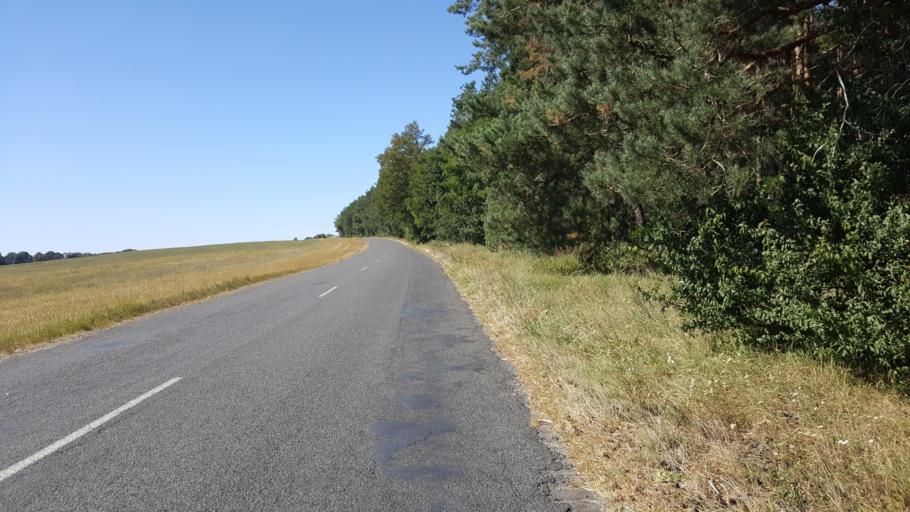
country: PL
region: Lublin Voivodeship
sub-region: Powiat bialski
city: Terespol
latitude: 52.2169
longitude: 23.5016
